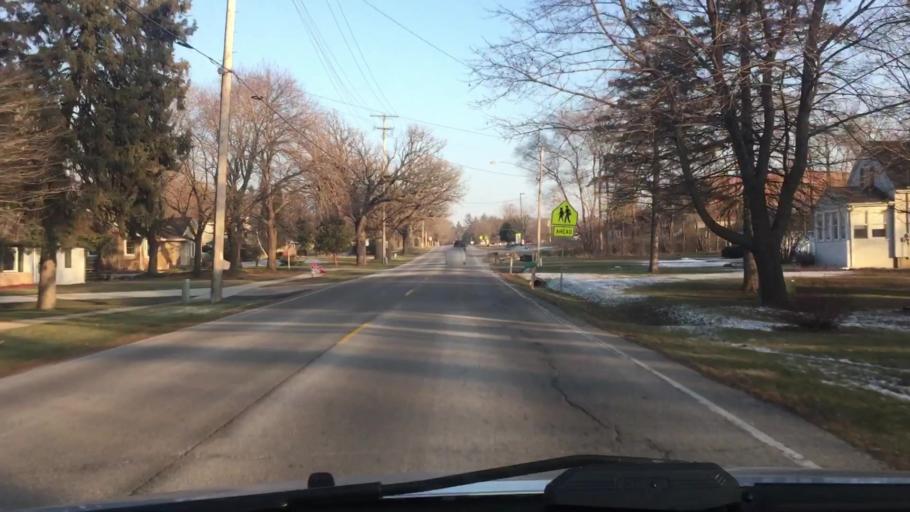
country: US
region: Wisconsin
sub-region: Waukesha County
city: Dousman
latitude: 43.0105
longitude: -88.4690
